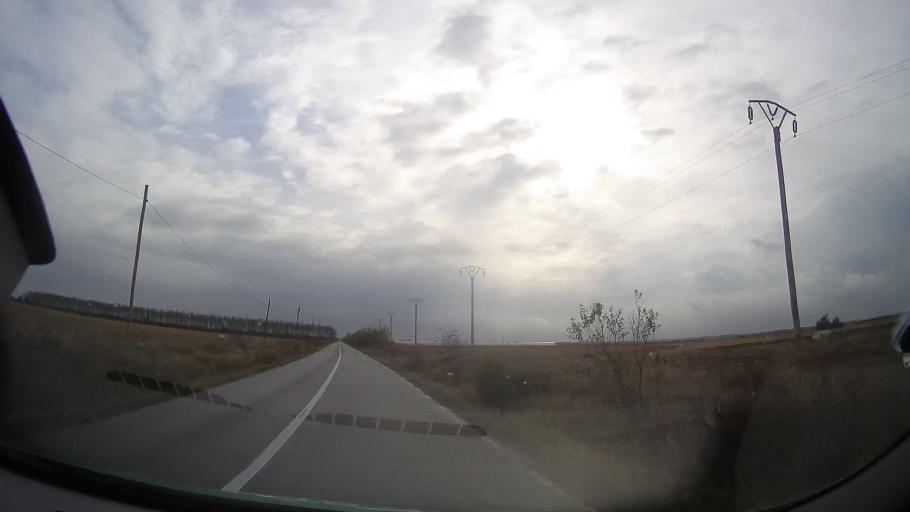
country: RO
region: Ialomita
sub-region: Comuna Maia
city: Maia
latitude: 44.7175
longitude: 26.3897
